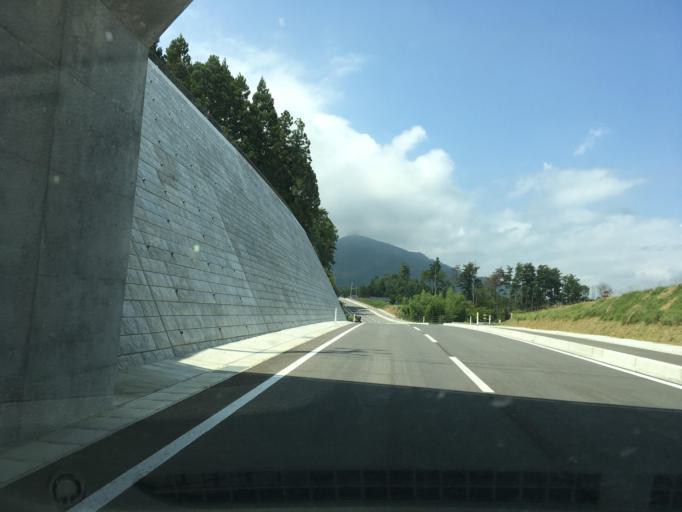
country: JP
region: Iwate
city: Ofunato
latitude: 39.0104
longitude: 141.7115
